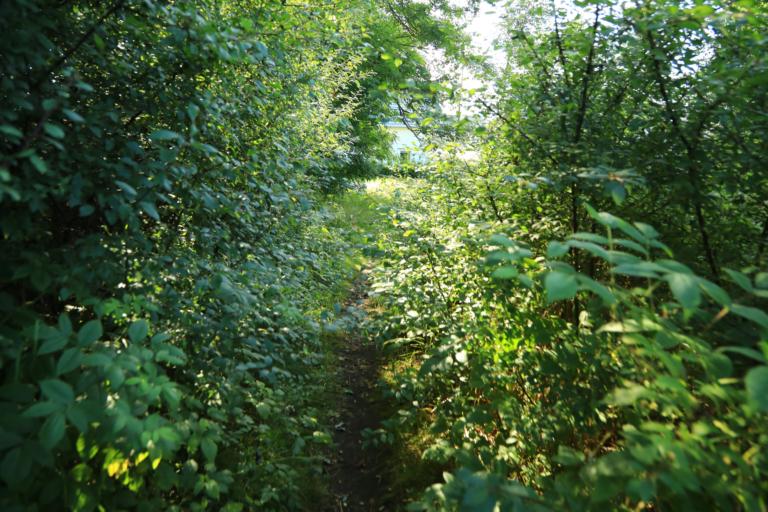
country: SE
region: Halland
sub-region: Varbergs Kommun
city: Varberg
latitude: 57.1545
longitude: 12.2582
